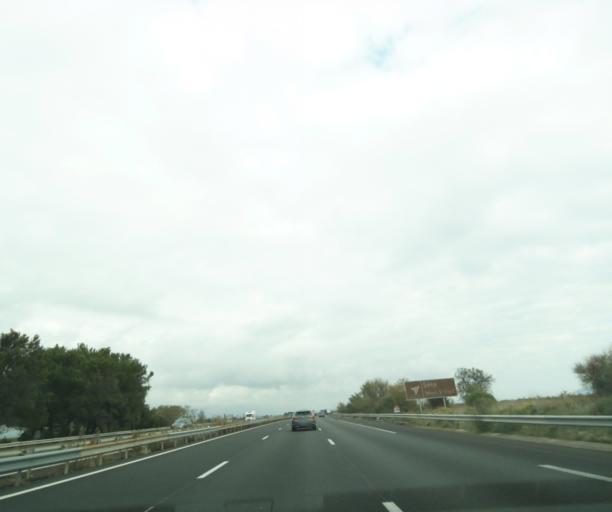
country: FR
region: Languedoc-Roussillon
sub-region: Departement de l'Herault
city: Pinet
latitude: 43.4182
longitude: 3.5258
